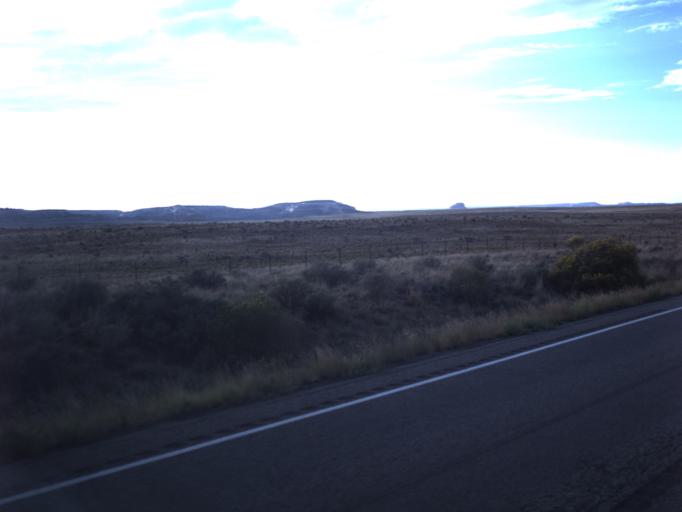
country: US
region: Utah
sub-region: San Juan County
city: Monticello
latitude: 38.1539
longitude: -109.3748
